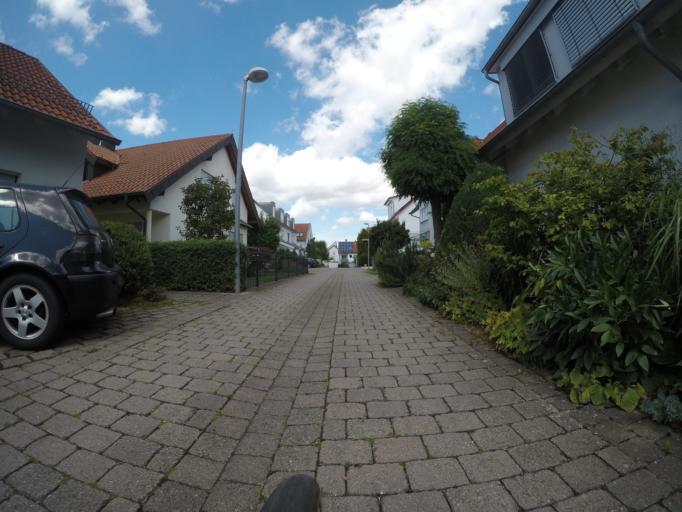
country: DE
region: Baden-Wuerttemberg
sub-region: Regierungsbezirk Stuttgart
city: Ehningen
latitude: 48.6887
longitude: 8.9356
